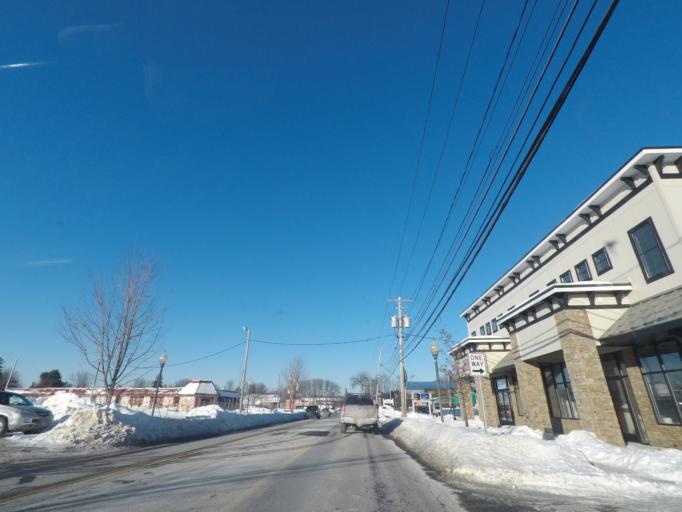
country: US
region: New York
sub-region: Saratoga County
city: Saratoga Springs
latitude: 43.0707
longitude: -73.7884
